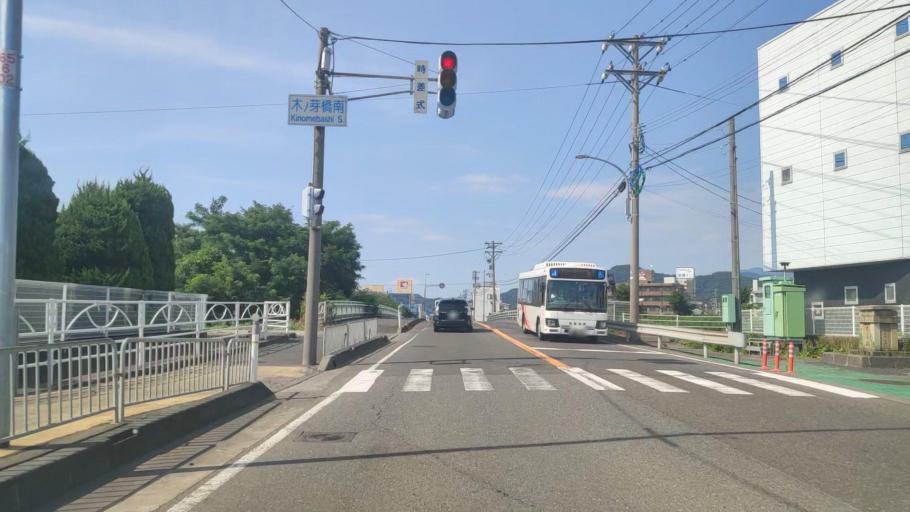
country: JP
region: Fukui
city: Tsuruga
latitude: 35.6418
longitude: 136.0712
